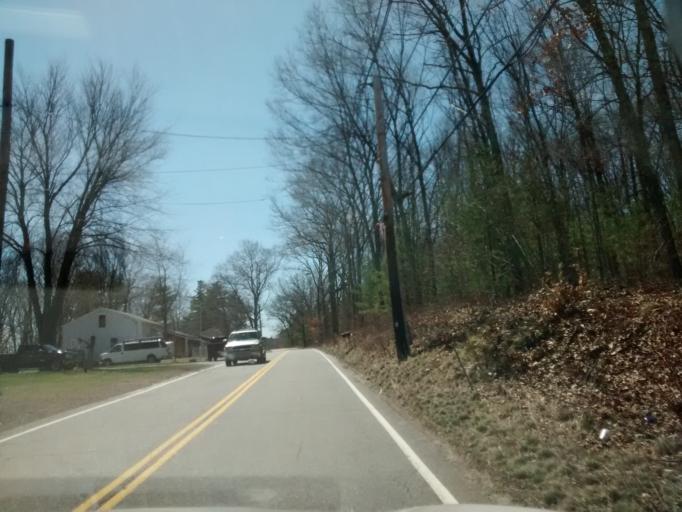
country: US
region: Massachusetts
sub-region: Worcester County
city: East Douglas
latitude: 42.0956
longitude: -71.6936
